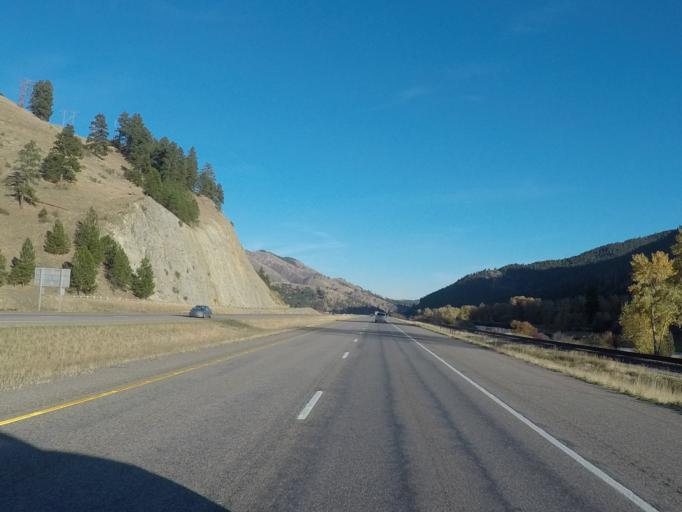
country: US
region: Montana
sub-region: Missoula County
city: Clinton
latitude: 46.7227
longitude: -113.5617
